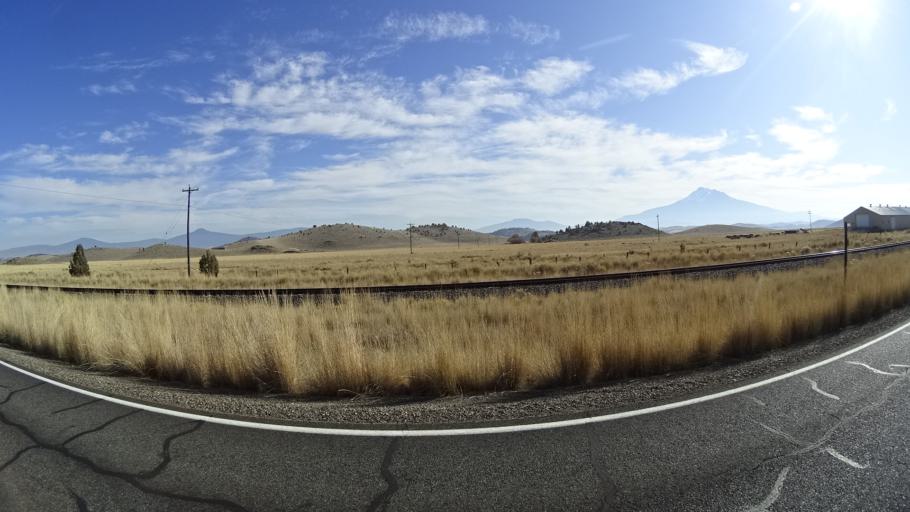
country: US
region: California
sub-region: Siskiyou County
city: Montague
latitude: 41.5845
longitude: -122.5245
